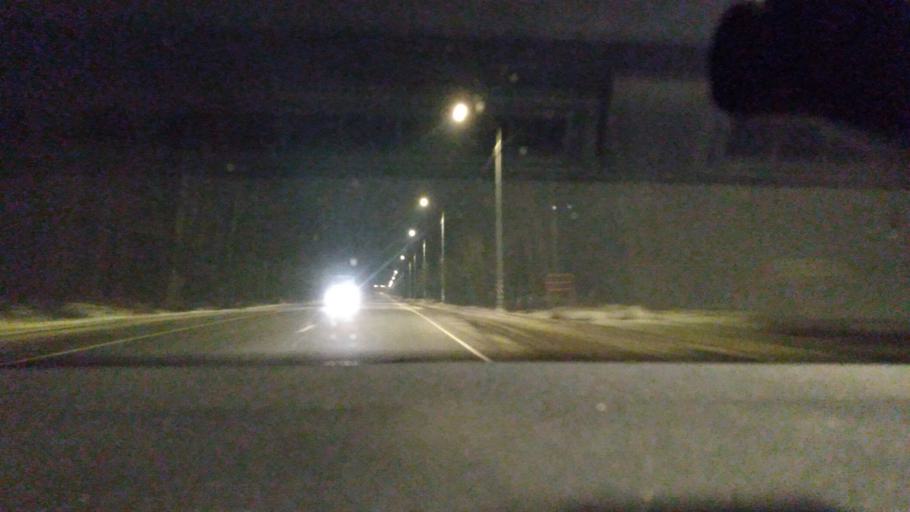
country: RU
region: Moskovskaya
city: Il'inskiy Pogost
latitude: 55.4678
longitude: 38.9678
